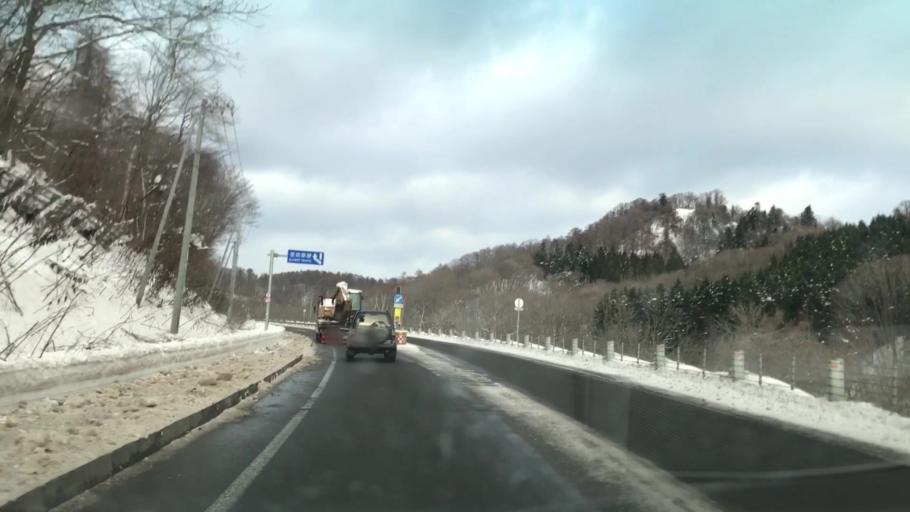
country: JP
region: Hokkaido
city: Yoichi
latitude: 43.2136
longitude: 140.7481
